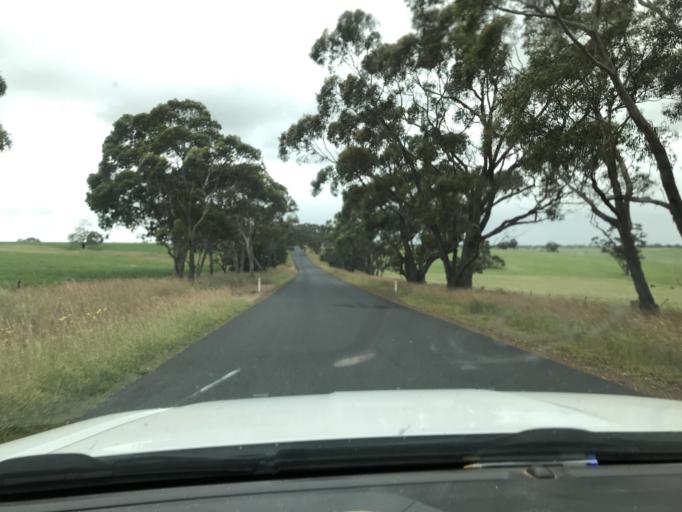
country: AU
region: Victoria
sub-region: Southern Grampians
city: Hamilton
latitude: -37.1821
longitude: 141.5621
